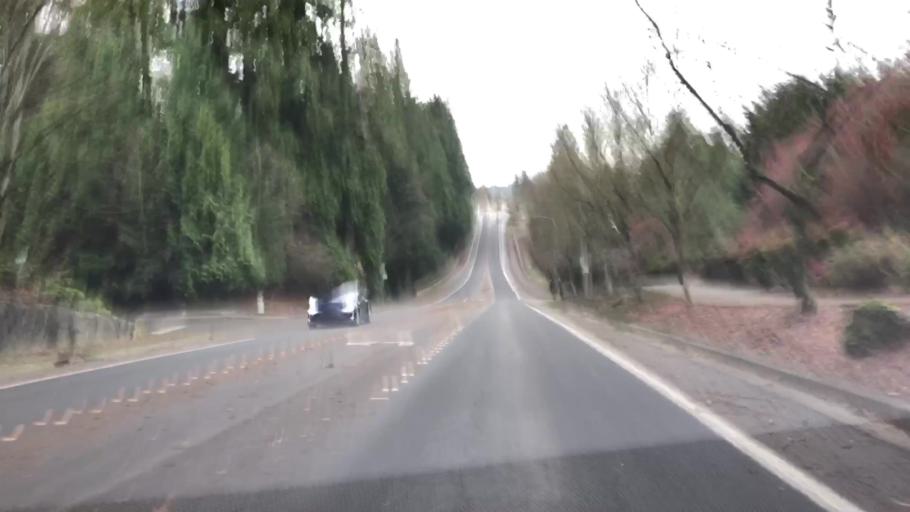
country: US
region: Washington
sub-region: King County
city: Redmond
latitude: 47.7039
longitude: -122.1179
